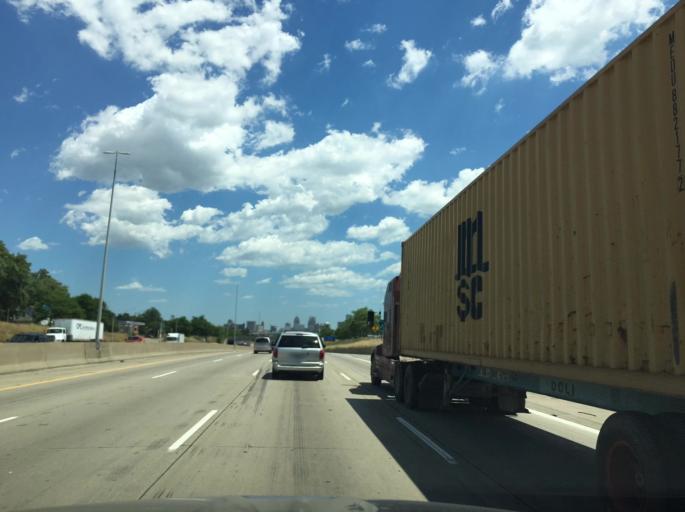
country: US
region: Michigan
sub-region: Wayne County
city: Detroit
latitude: 42.3121
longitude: -83.0945
